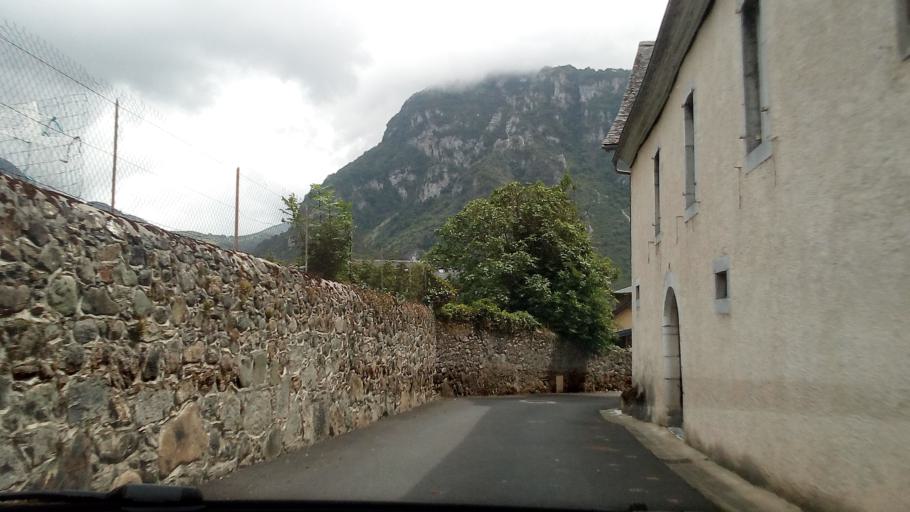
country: FR
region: Aquitaine
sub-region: Departement des Pyrenees-Atlantiques
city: Louvie-Juzon
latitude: 43.0558
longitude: -0.4353
